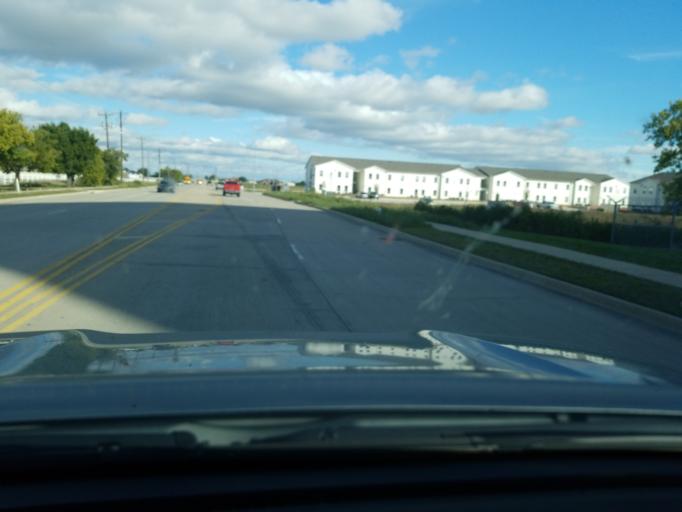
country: US
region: Texas
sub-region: Tarrant County
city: Haslet
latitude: 32.9688
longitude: -97.4102
